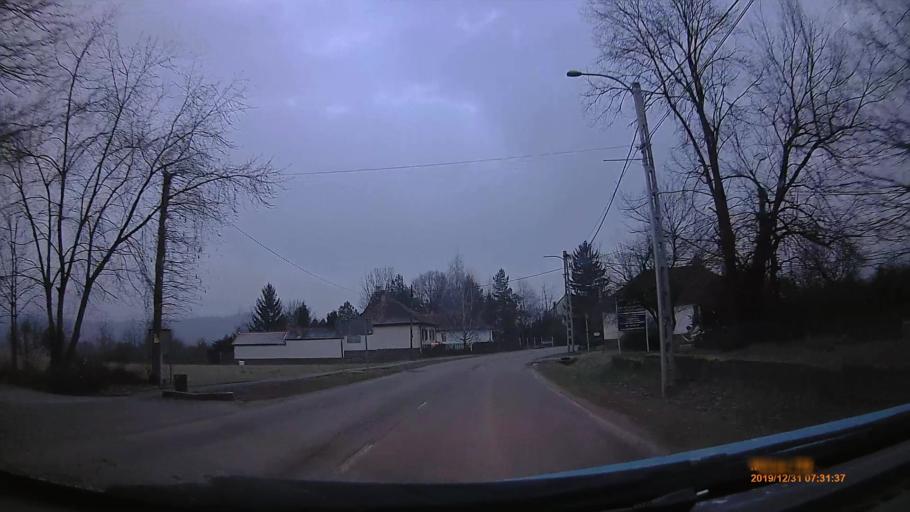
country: HU
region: Heves
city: Recsk
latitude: 47.9349
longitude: 20.1177
